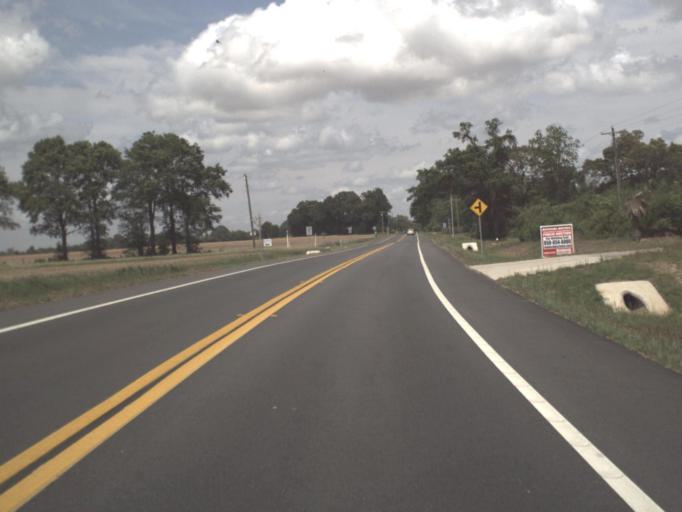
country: US
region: Florida
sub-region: Escambia County
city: Century
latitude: 30.9131
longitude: -87.1677
